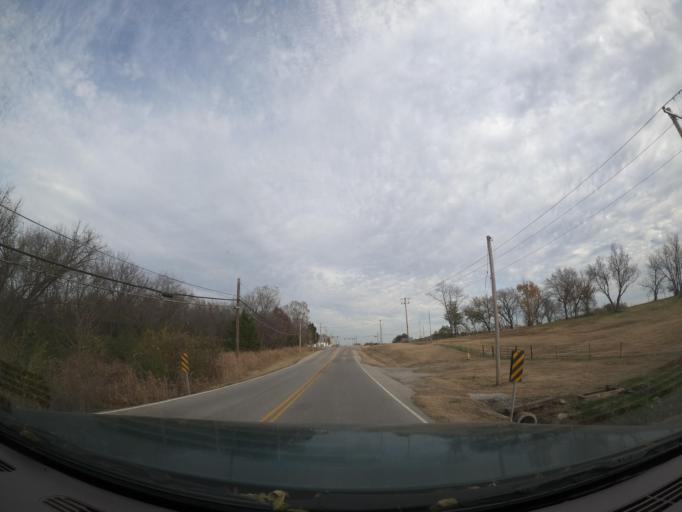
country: US
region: Oklahoma
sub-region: Tulsa County
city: Turley
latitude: 36.2061
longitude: -95.9608
